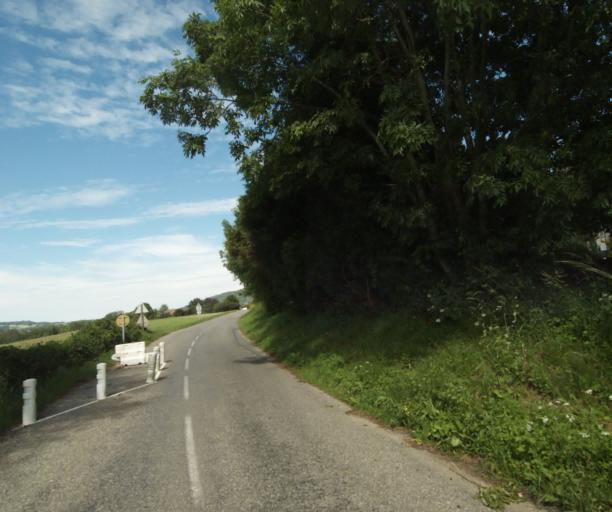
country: FR
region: Rhone-Alpes
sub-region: Departement de la Haute-Savoie
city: Perrignier
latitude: 46.2807
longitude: 6.4285
